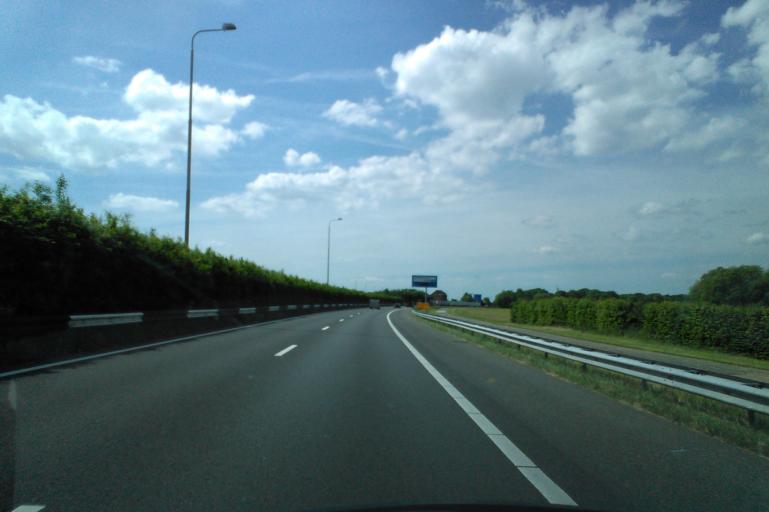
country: NL
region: Limburg
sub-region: Gemeente Meerssen
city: Meerssen
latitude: 50.9031
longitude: 5.7572
